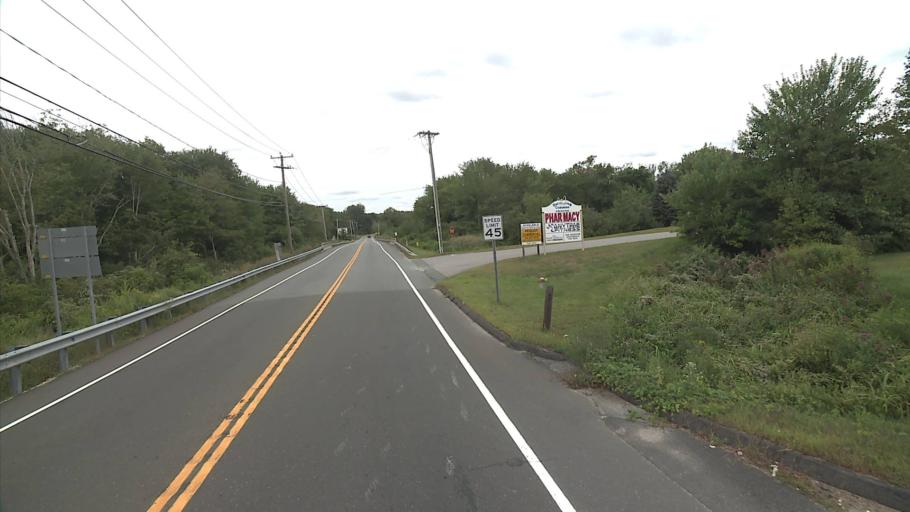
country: US
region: Connecticut
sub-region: New London County
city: Montville Center
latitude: 41.4774
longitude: -72.2656
